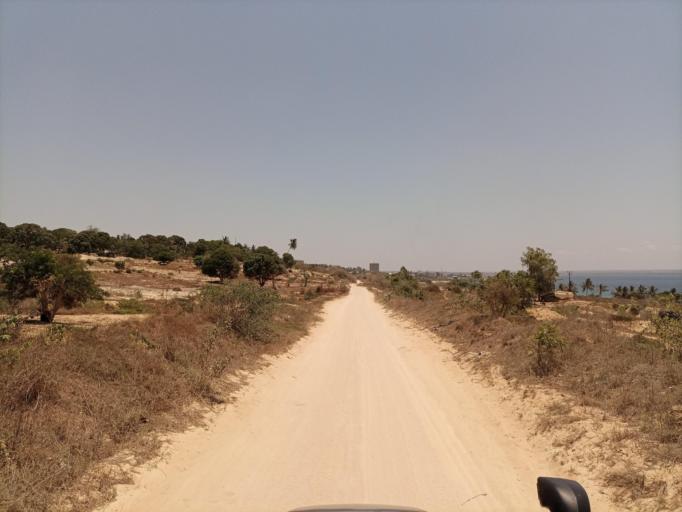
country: MZ
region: Nampula
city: Nacala
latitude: -14.5213
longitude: 40.6794
